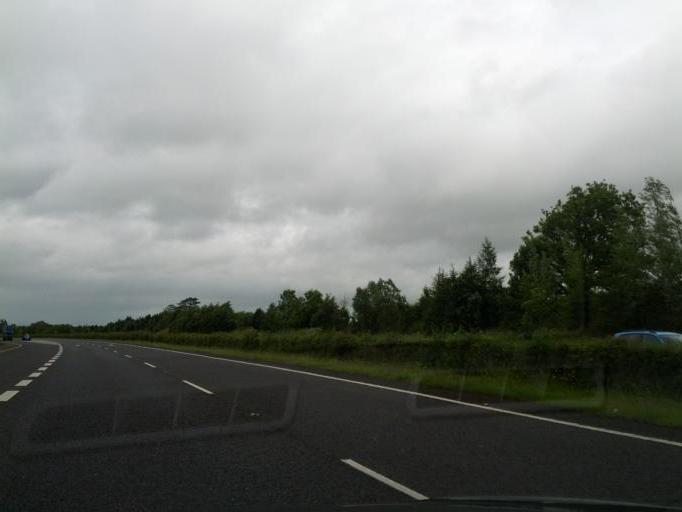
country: IE
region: Munster
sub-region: An Clar
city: Newmarket on Fergus
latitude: 52.7476
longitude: -8.8971
